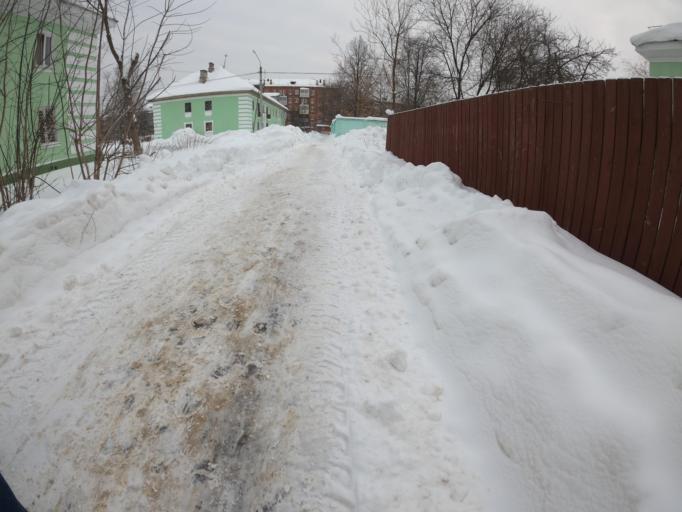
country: RU
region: Moskovskaya
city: Elektrogorsk
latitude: 55.8768
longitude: 38.7846
